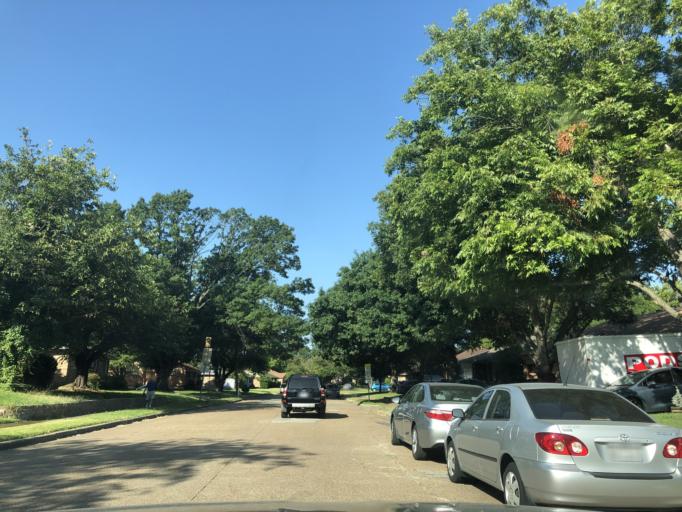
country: US
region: Texas
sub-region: Dallas County
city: Garland
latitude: 32.8674
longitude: -96.6454
